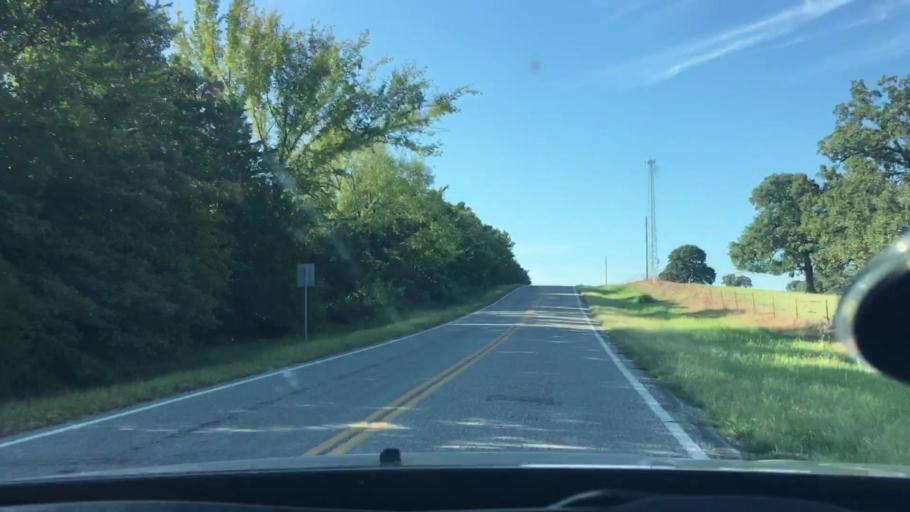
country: US
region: Oklahoma
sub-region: Coal County
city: Coalgate
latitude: 34.6172
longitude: -96.4244
